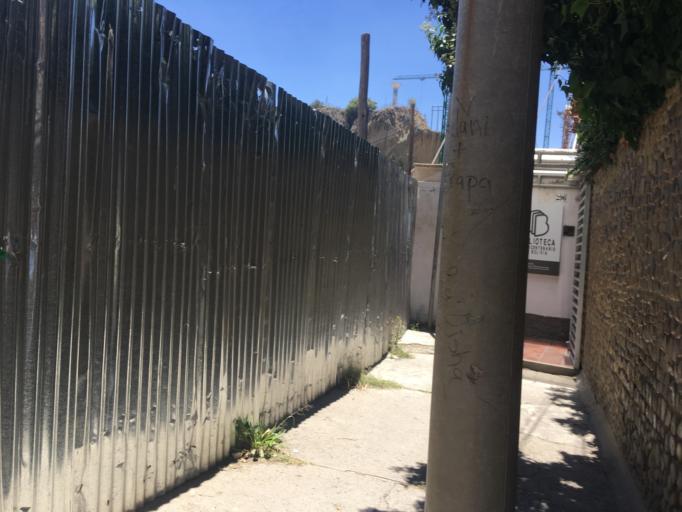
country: BO
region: La Paz
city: La Paz
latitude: -16.5075
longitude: -68.1245
